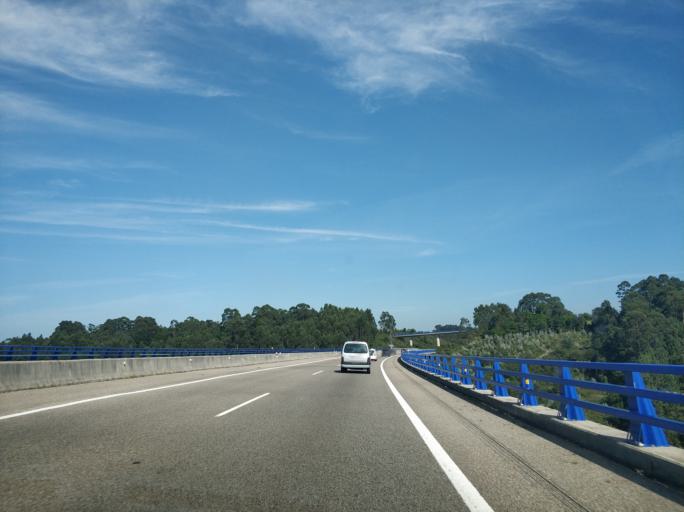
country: ES
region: Asturias
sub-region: Province of Asturias
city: Castrillon
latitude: 43.5481
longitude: -5.9758
